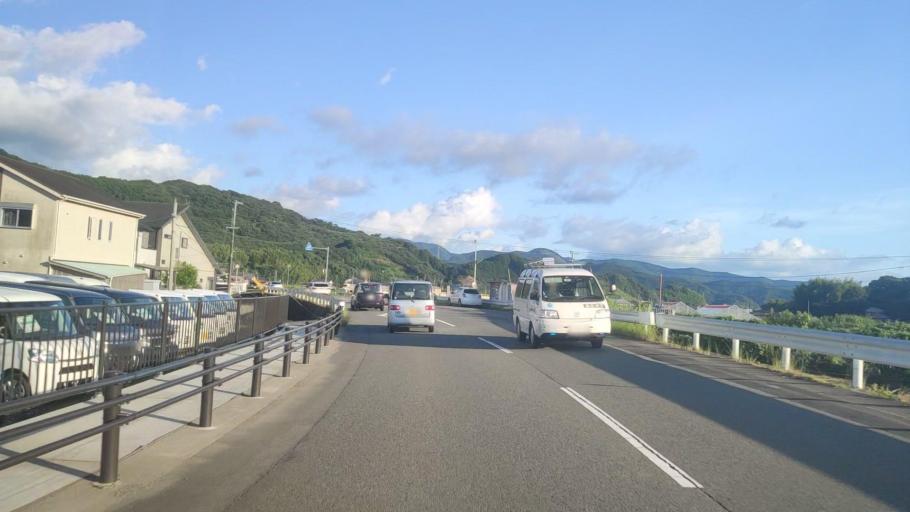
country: JP
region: Wakayama
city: Tanabe
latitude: 33.7185
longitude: 135.4460
